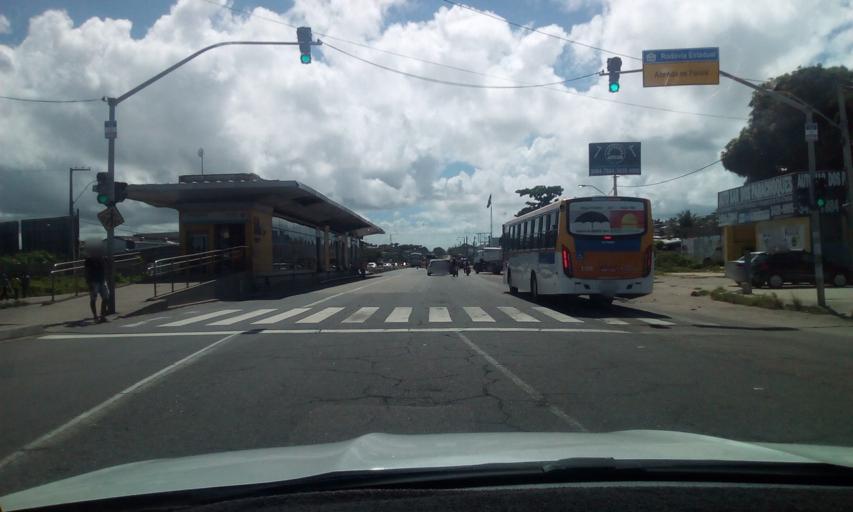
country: BR
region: Pernambuco
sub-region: Olinda
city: Olinda
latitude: -8.0154
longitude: -34.8599
